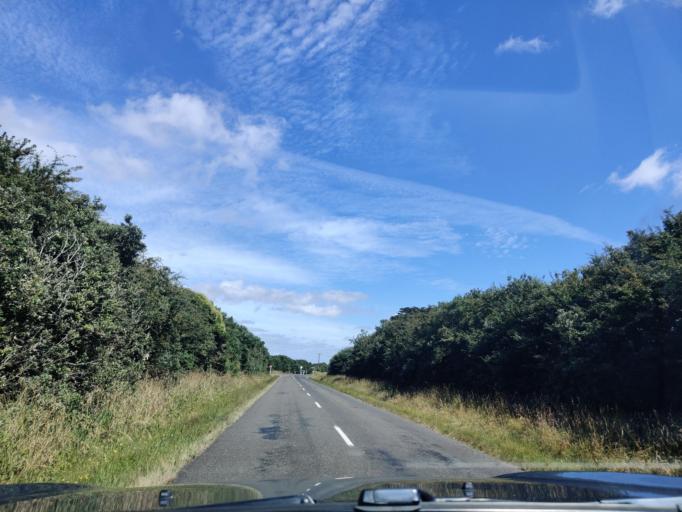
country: NZ
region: Manawatu-Wanganui
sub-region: Rangitikei District
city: Bulls
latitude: -40.1806
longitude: 175.4339
